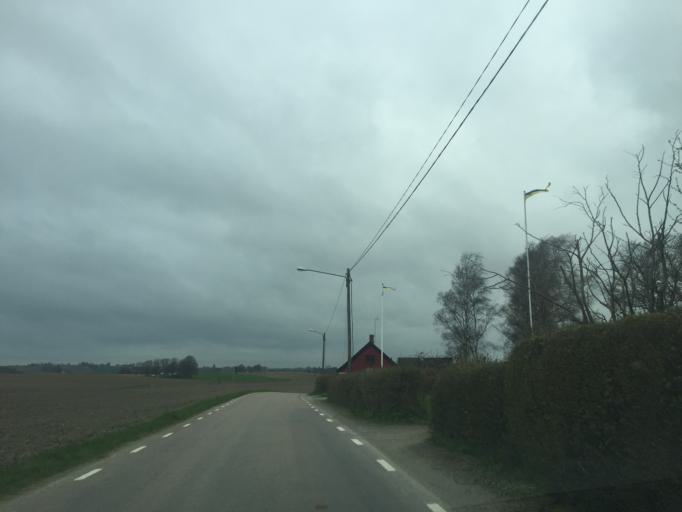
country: SE
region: Skane
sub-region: Skurups Kommun
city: Rydsgard
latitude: 55.4544
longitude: 13.6190
